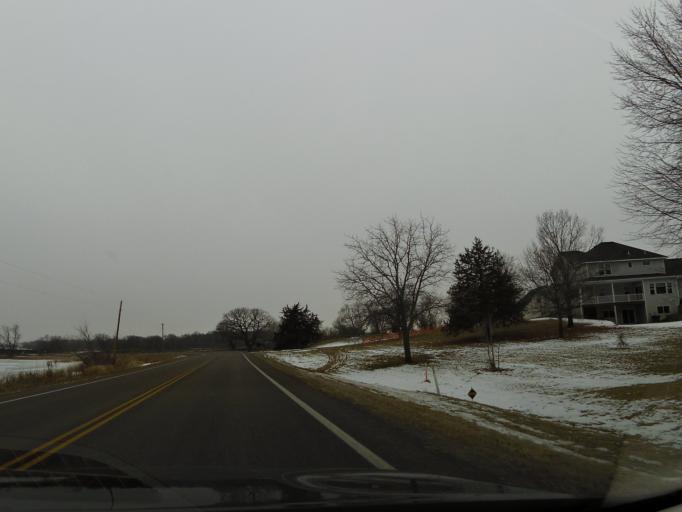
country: US
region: Minnesota
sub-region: Scott County
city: Prior Lake
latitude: 44.6293
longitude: -93.4820
